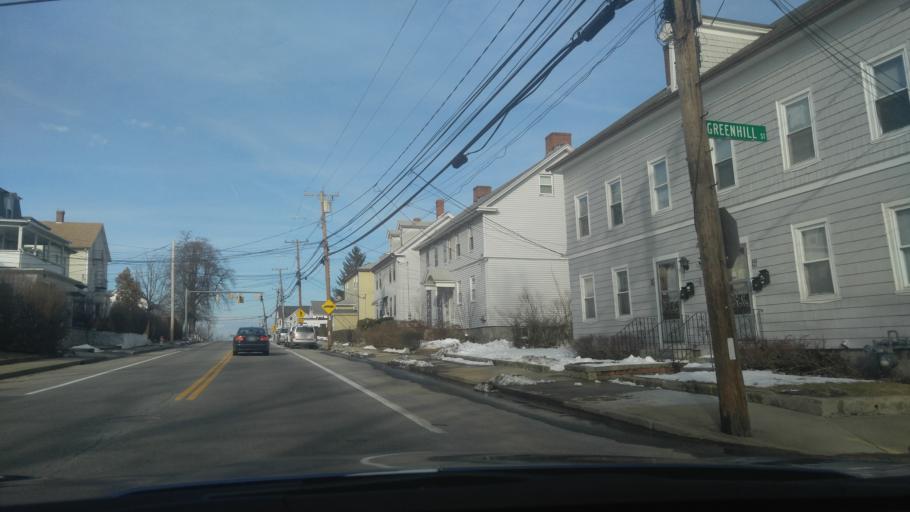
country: US
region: Rhode Island
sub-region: Kent County
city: West Warwick
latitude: 41.7182
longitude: -71.4925
